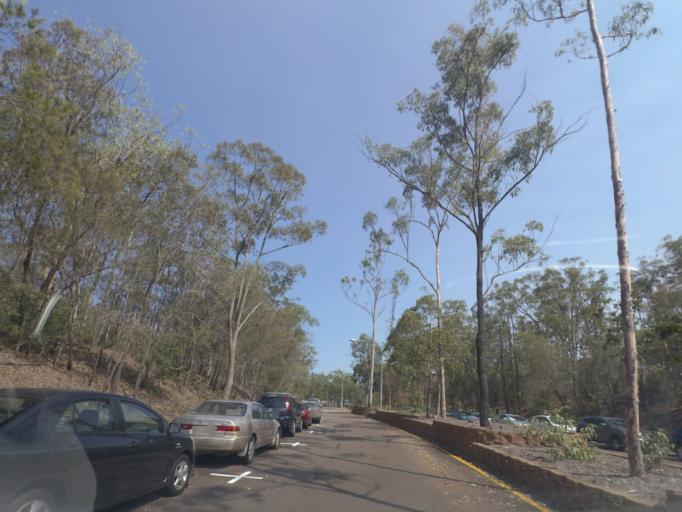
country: AU
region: Queensland
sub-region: Brisbane
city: Nathan
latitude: -27.5512
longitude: 153.0489
